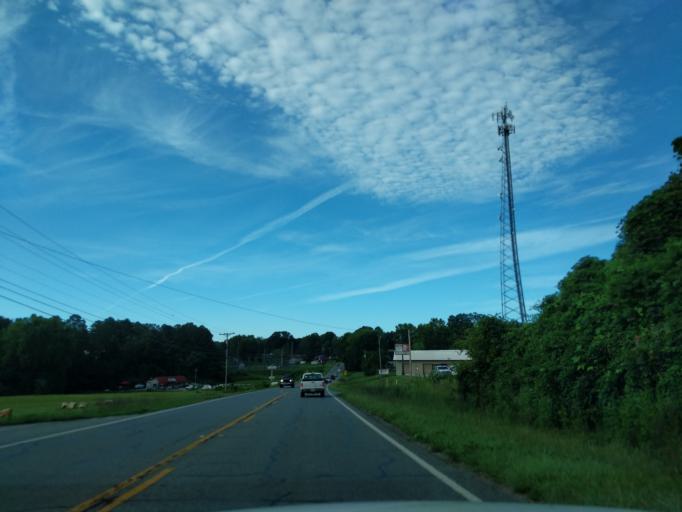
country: US
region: Georgia
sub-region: Fannin County
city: McCaysville
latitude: 34.9521
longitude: -84.3689
